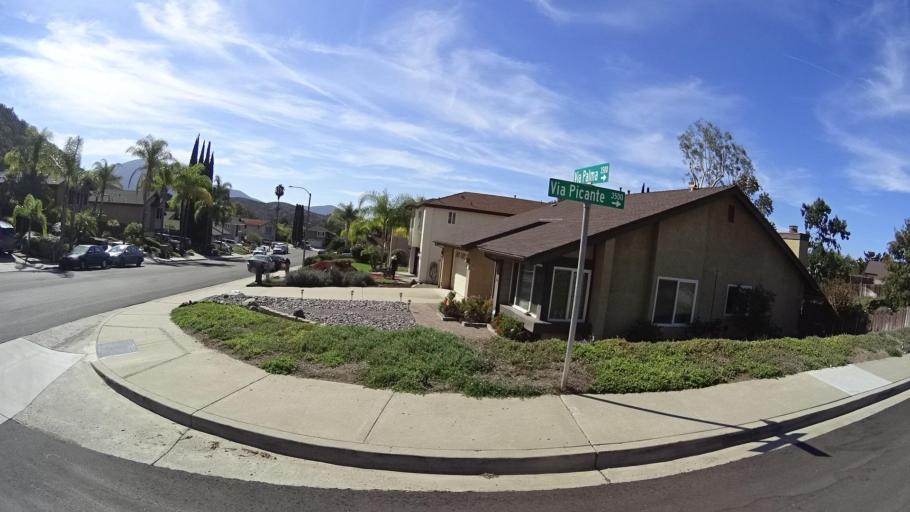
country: US
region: California
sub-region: San Diego County
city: Rancho San Diego
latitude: 32.7463
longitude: -116.9533
